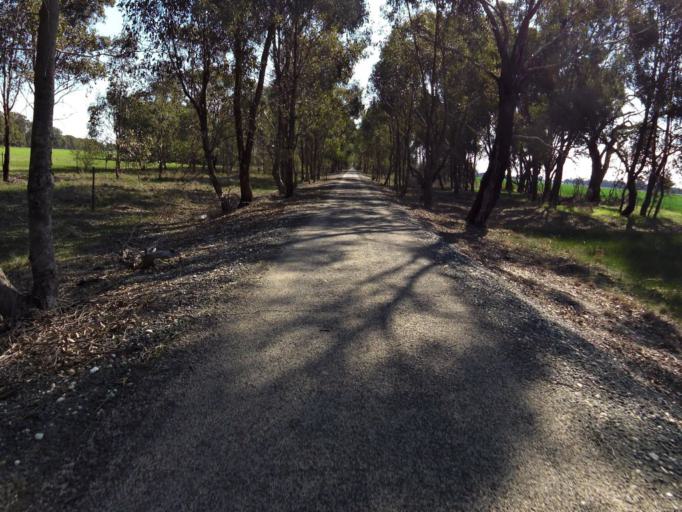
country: AU
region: New South Wales
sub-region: Corowa Shire
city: Corowa
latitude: -36.0264
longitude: 146.4331
